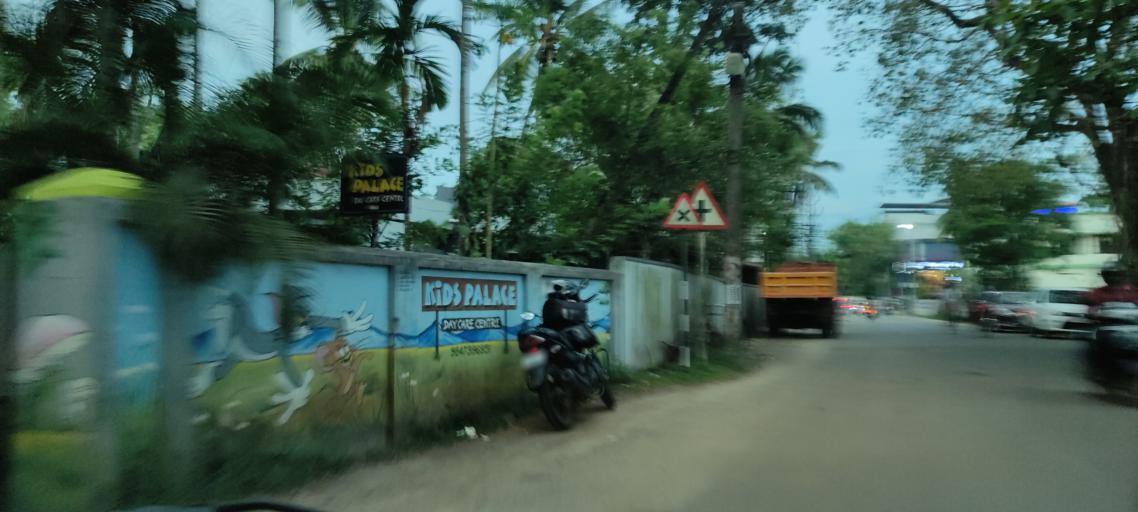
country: IN
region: Kerala
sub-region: Alappuzha
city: Shertallai
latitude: 9.6867
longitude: 76.3449
